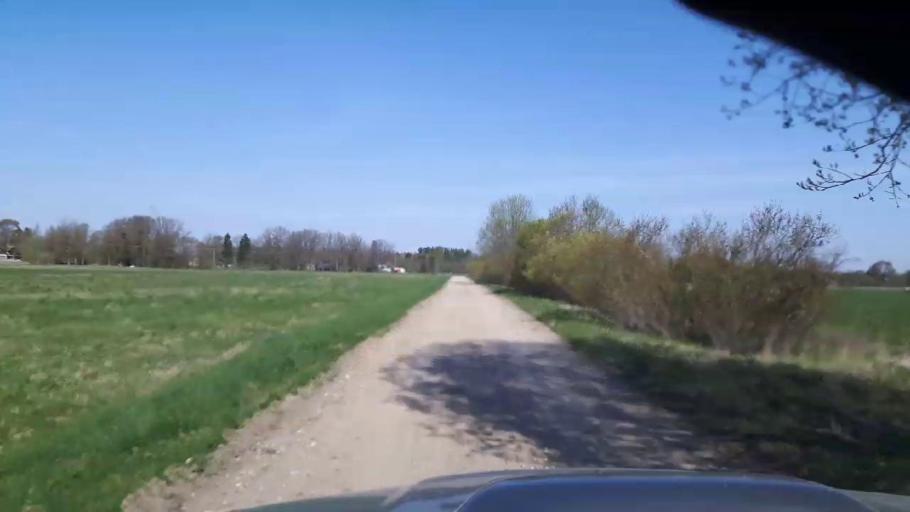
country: EE
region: Paernumaa
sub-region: Tootsi vald
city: Tootsi
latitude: 58.4874
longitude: 24.9277
